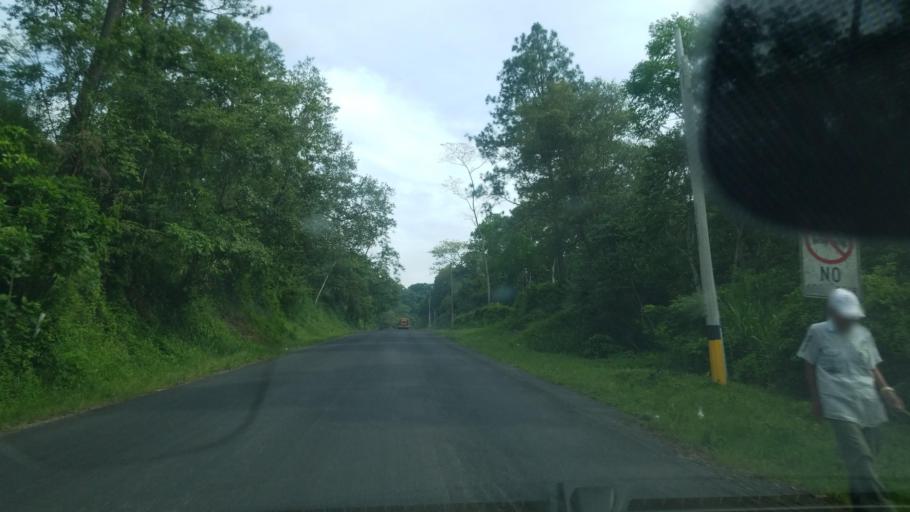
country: HN
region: Santa Barbara
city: Petoa
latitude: 15.2226
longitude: -88.2674
